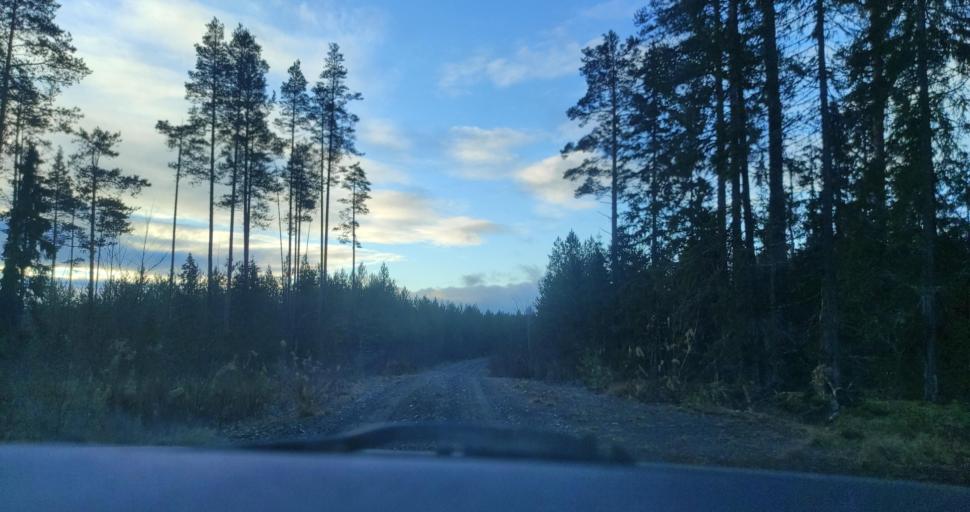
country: RU
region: Republic of Karelia
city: Pitkyaranta
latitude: 61.7396
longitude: 31.3645
